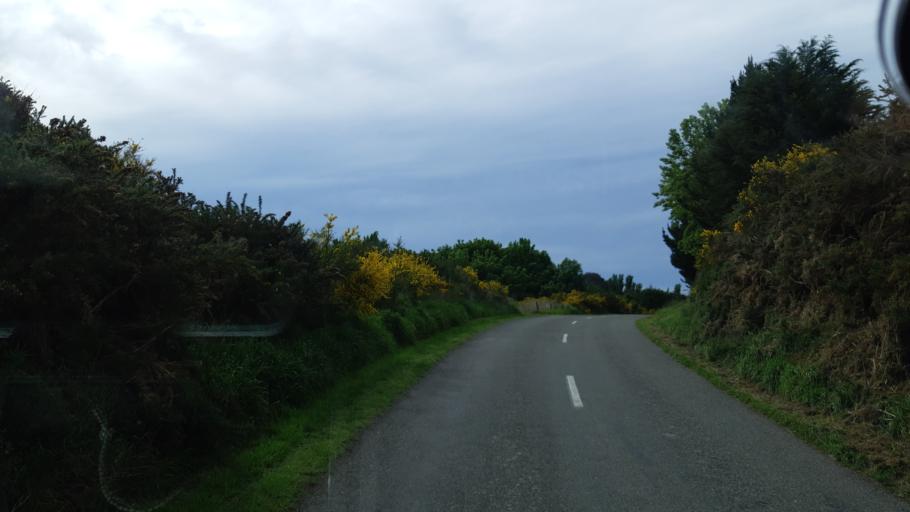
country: NZ
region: Canterbury
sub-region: Timaru District
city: Timaru
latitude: -44.5451
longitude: 171.1739
